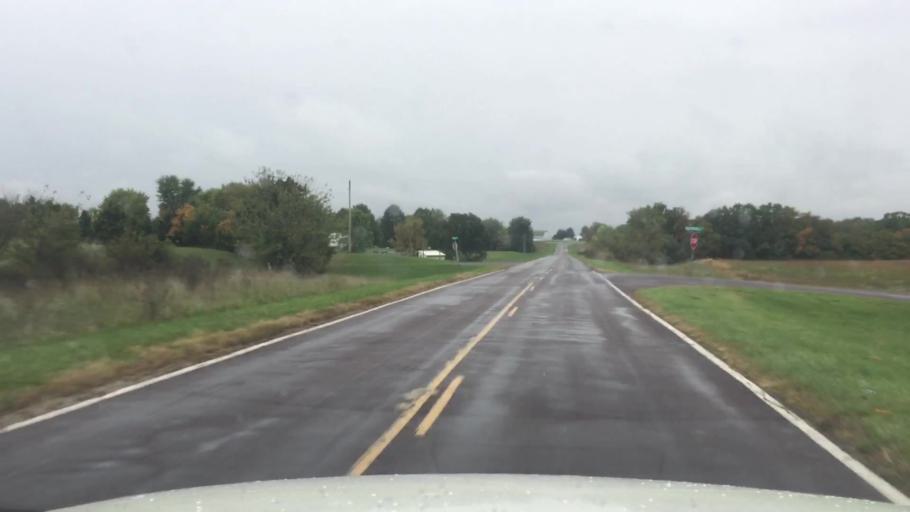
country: US
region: Missouri
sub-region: Boone County
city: Ashland
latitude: 38.7266
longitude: -92.2630
